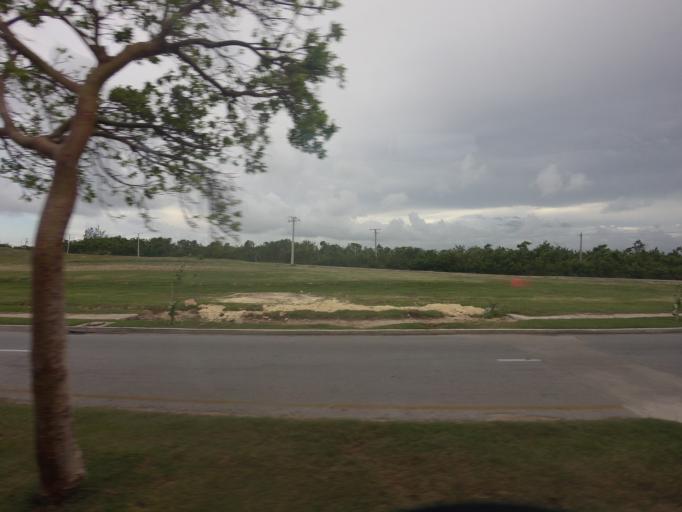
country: CU
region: Matanzas
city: Varadero
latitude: 23.1961
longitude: -81.1426
